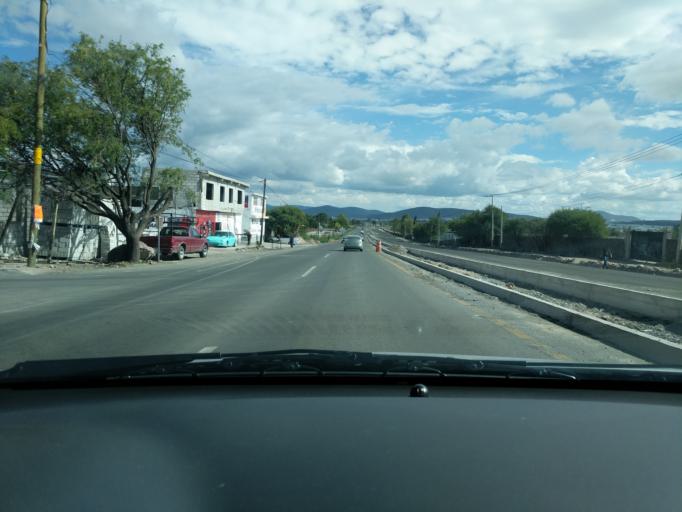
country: MX
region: Queretaro
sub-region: El Marques
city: Paseos del Marques
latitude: 20.6007
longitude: -100.2465
